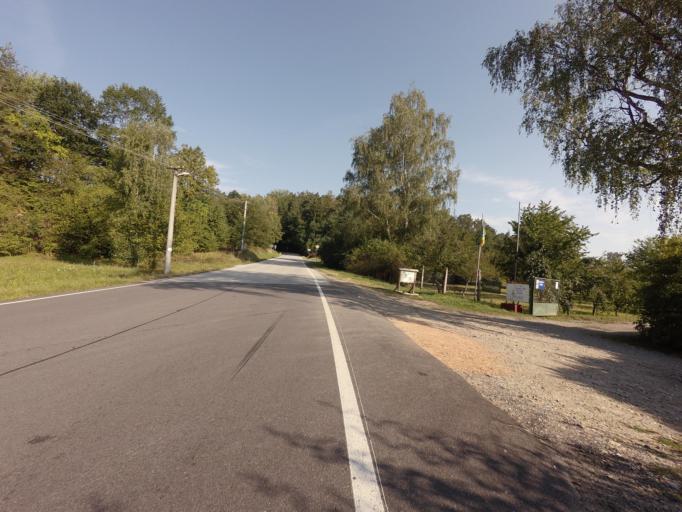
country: CZ
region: Jihocesky
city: Tyn nad Vltavou
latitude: 49.2542
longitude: 14.4199
